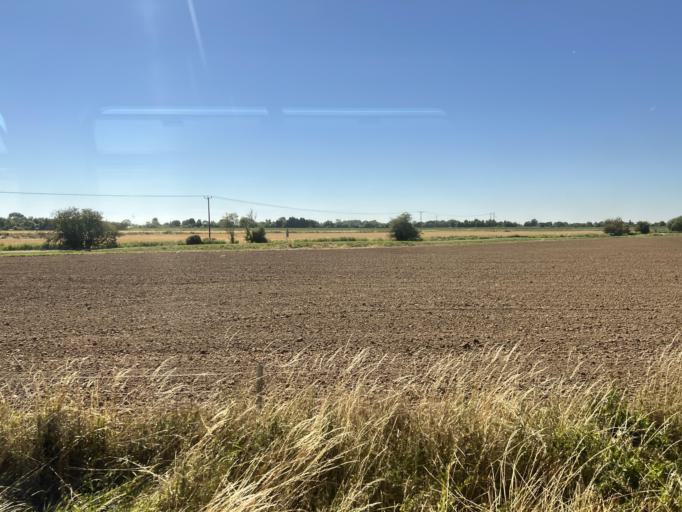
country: GB
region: England
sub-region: Lincolnshire
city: Wainfleet All Saints
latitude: 53.1154
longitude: 0.2125
